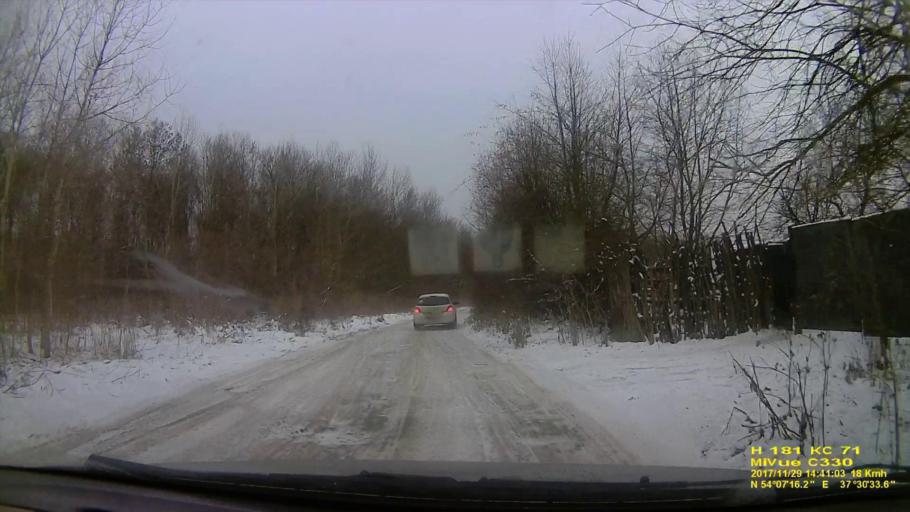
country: RU
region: Tula
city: Kosaya Gora
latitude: 54.1212
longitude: 37.5092
